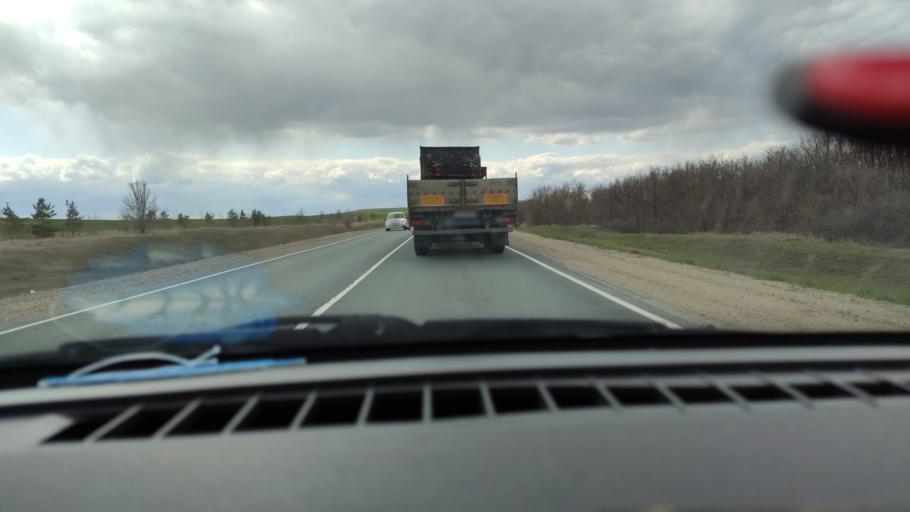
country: RU
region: Saratov
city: Alekseyevka
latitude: 52.2306
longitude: 47.9026
